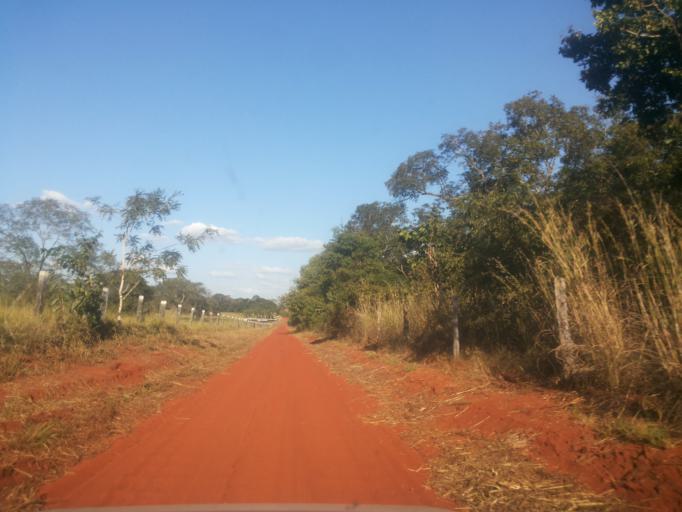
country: BR
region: Minas Gerais
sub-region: Santa Vitoria
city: Santa Vitoria
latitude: -19.0222
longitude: -50.4394
